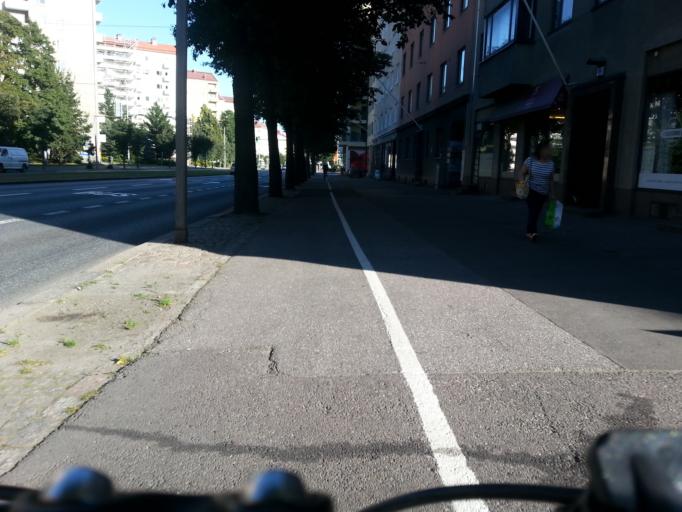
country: FI
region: Uusimaa
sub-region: Helsinki
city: Helsinki
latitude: 60.1927
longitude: 24.9084
